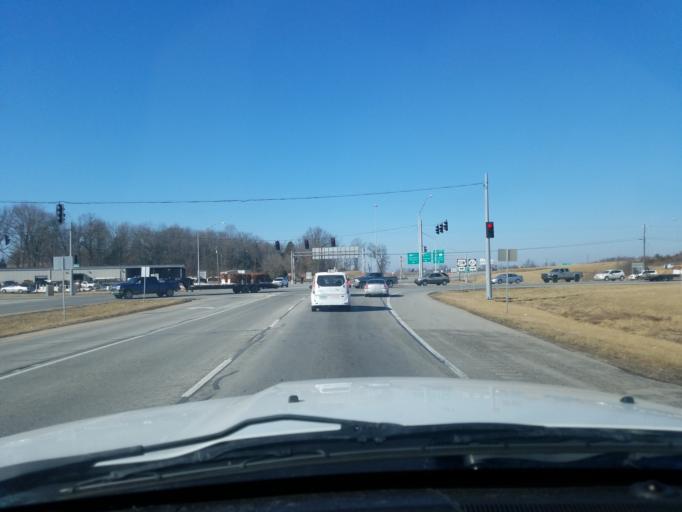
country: US
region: Kentucky
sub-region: Hardin County
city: Elizabethtown
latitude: 37.6697
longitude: -85.8458
